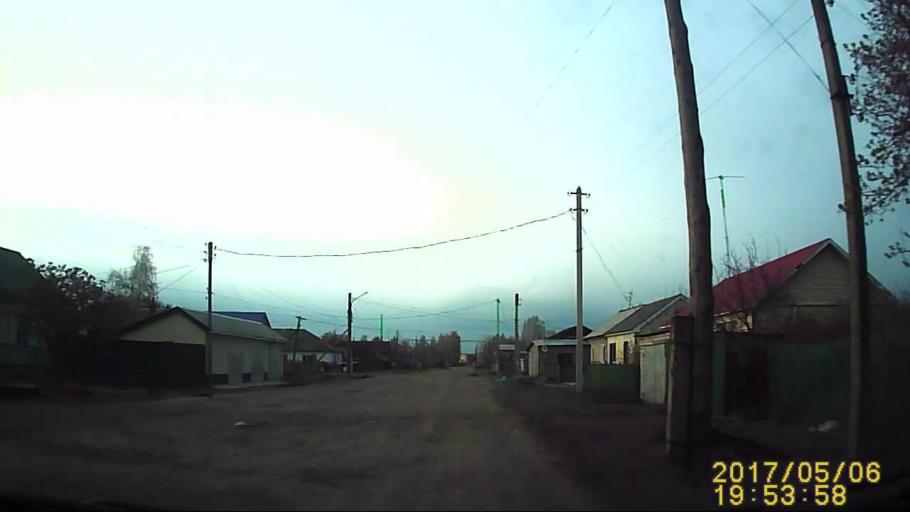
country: RU
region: Ulyanovsk
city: Staraya Mayna
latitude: 54.6024
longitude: 48.9367
